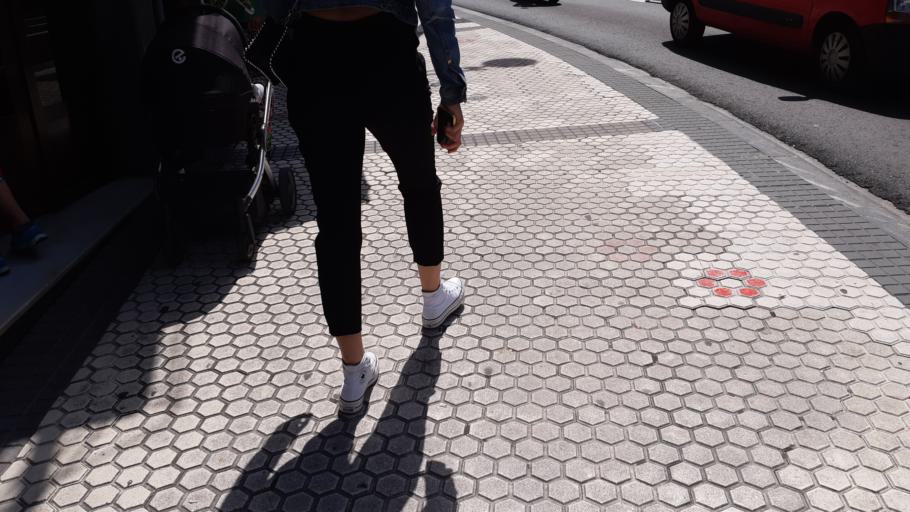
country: ES
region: Basque Country
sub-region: Provincia de Guipuzcoa
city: San Sebastian
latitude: 43.3166
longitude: -1.9745
